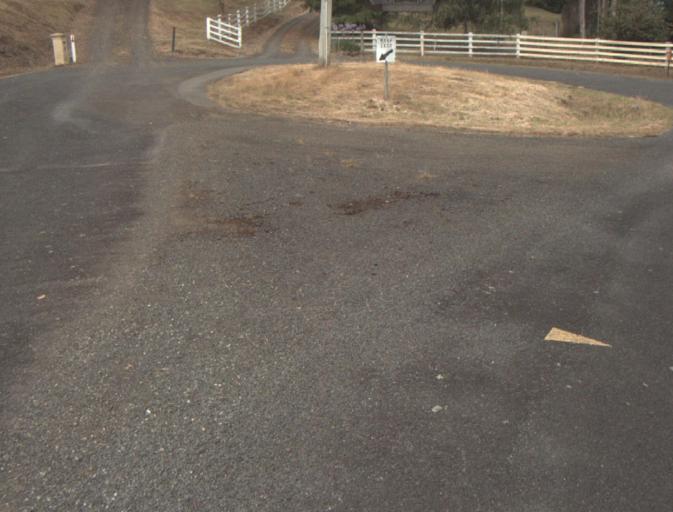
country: AU
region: Tasmania
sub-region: Launceston
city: Mayfield
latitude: -41.2796
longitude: 147.0223
